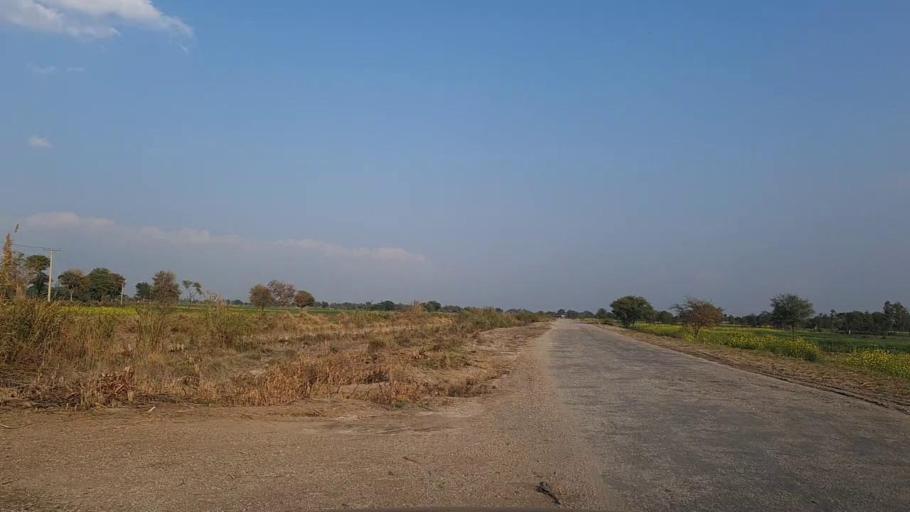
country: PK
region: Sindh
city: Jam Sahib
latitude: 26.3532
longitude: 68.5697
